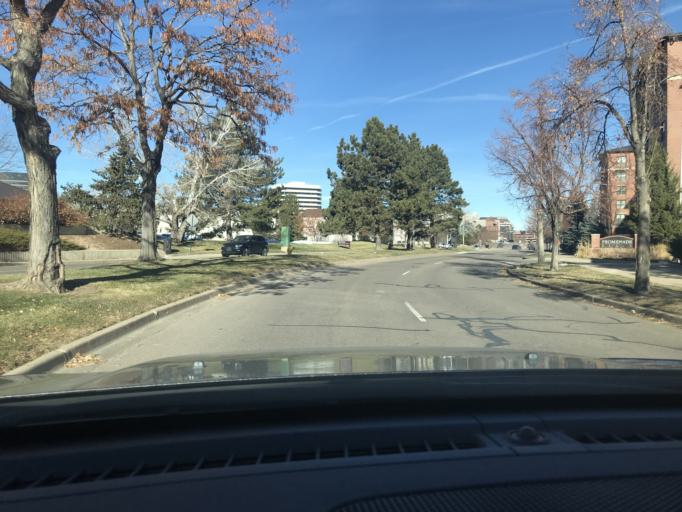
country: US
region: Colorado
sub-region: Arapahoe County
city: Castlewood
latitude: 39.6209
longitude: -104.8946
